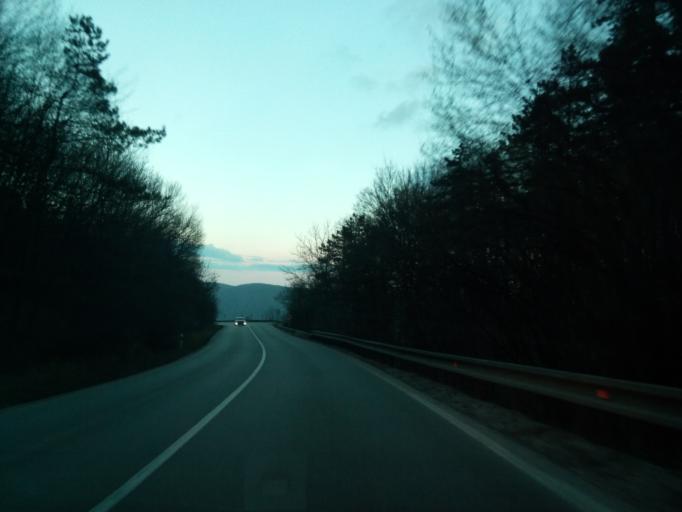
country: SK
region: Kosicky
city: Roznava
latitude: 48.6034
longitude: 20.6388
